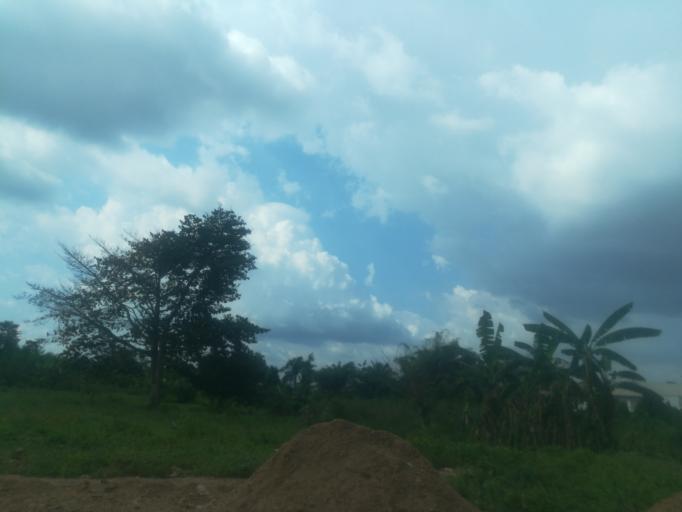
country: NG
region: Oyo
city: Ido
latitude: 7.4119
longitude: 3.8165
